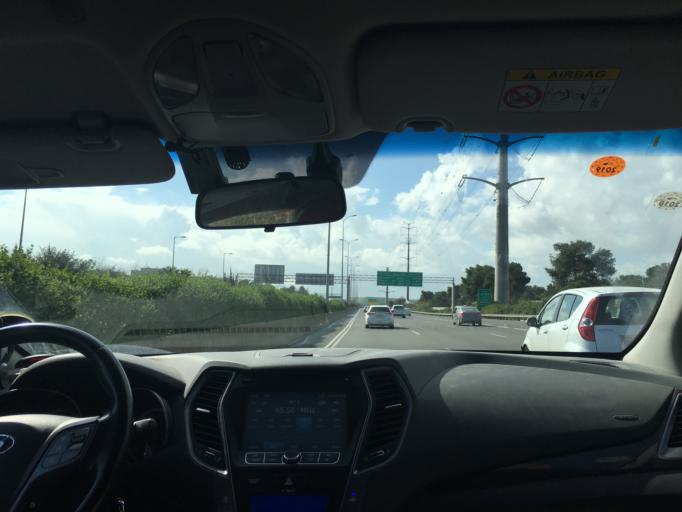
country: IL
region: Tel Aviv
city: Giv`atayim
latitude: 32.0518
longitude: 34.8321
